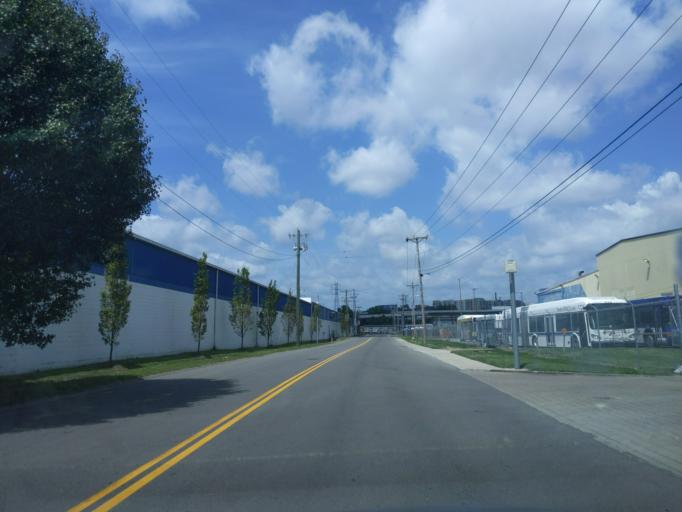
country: US
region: Tennessee
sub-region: Davidson County
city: Nashville
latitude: 36.1569
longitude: -86.7542
